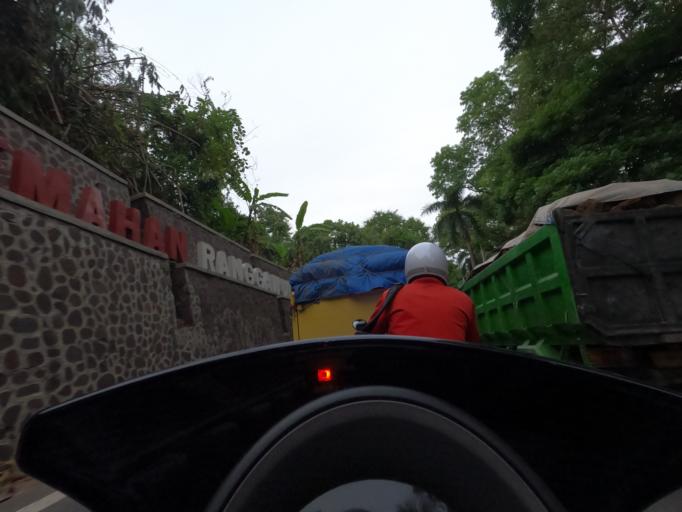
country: ID
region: West Java
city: Lembang
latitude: -6.5791
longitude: 107.7480
